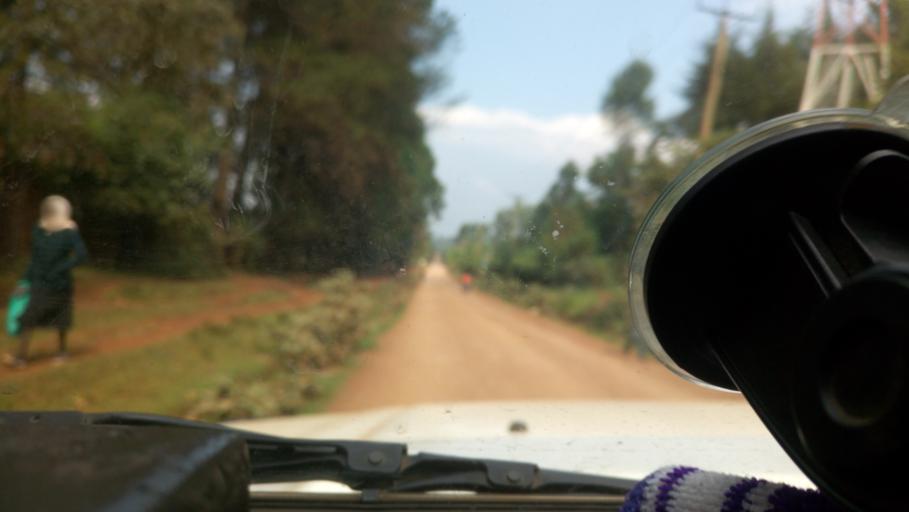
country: KE
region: Kericho
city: Litein
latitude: -0.6271
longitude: 35.1939
